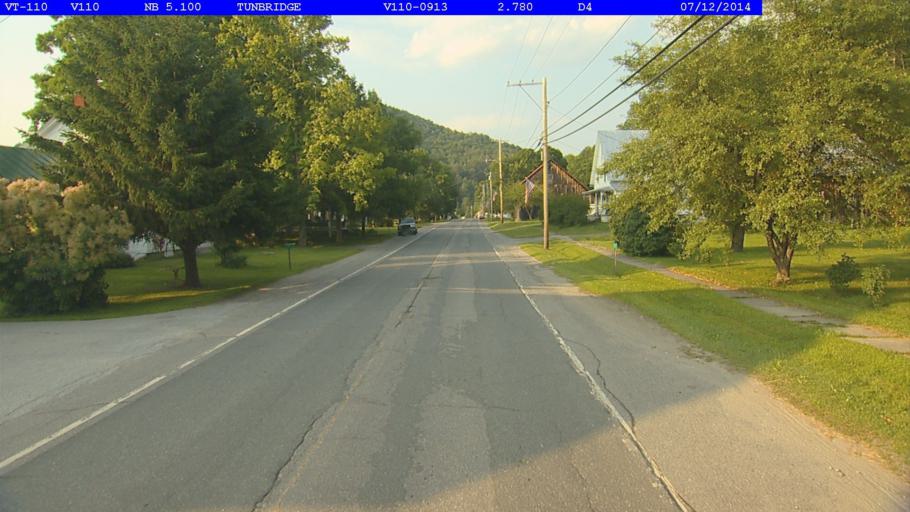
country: US
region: Vermont
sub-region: Orange County
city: Chelsea
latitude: 43.8881
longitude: -72.4936
